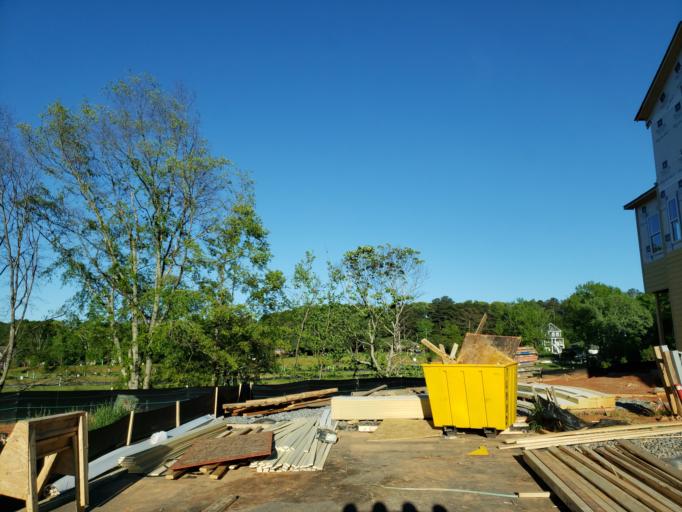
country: US
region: Georgia
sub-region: Cobb County
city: Smyrna
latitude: 33.8923
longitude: -84.5130
